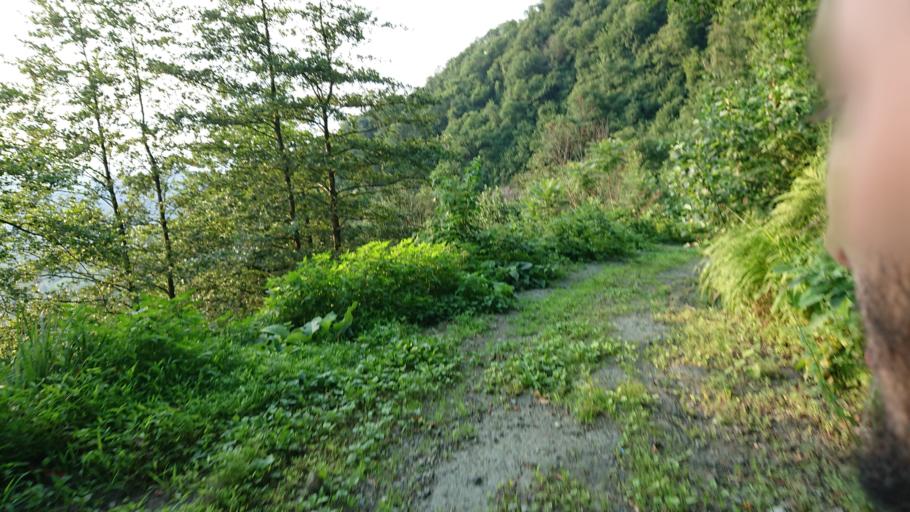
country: TR
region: Rize
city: Rize
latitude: 40.9887
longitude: 40.5034
